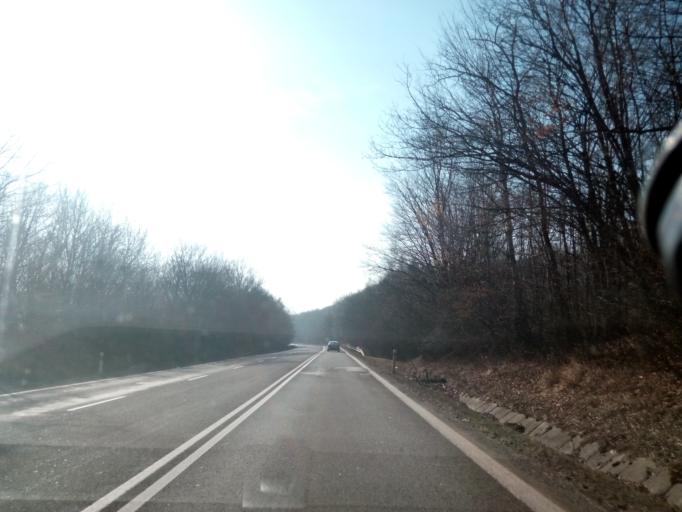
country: SK
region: Kosicky
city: Kosice
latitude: 48.7319
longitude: 21.3223
